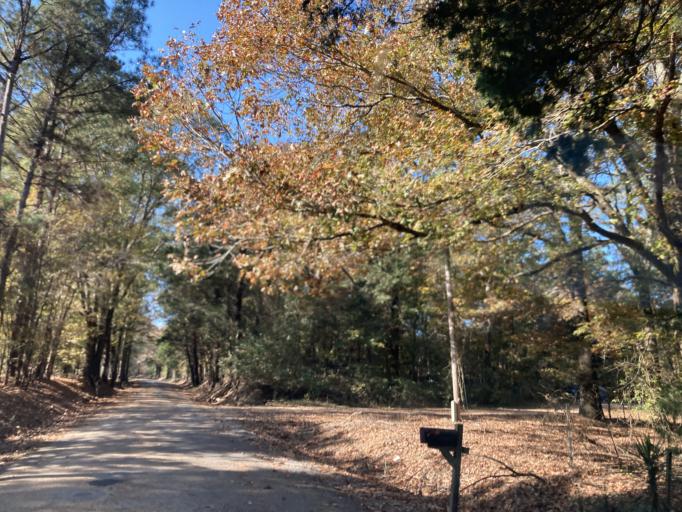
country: US
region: Mississippi
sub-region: Yazoo County
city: Yazoo City
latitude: 32.7452
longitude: -90.3301
